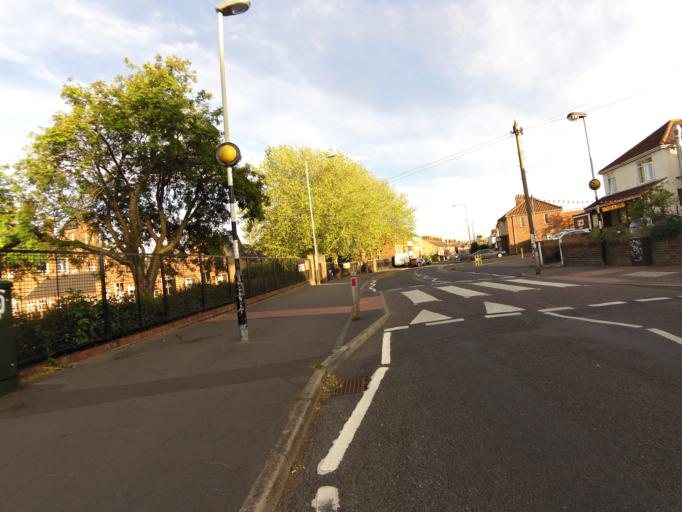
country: GB
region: England
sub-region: Norfolk
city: Norwich
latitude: 52.6434
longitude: 1.2922
